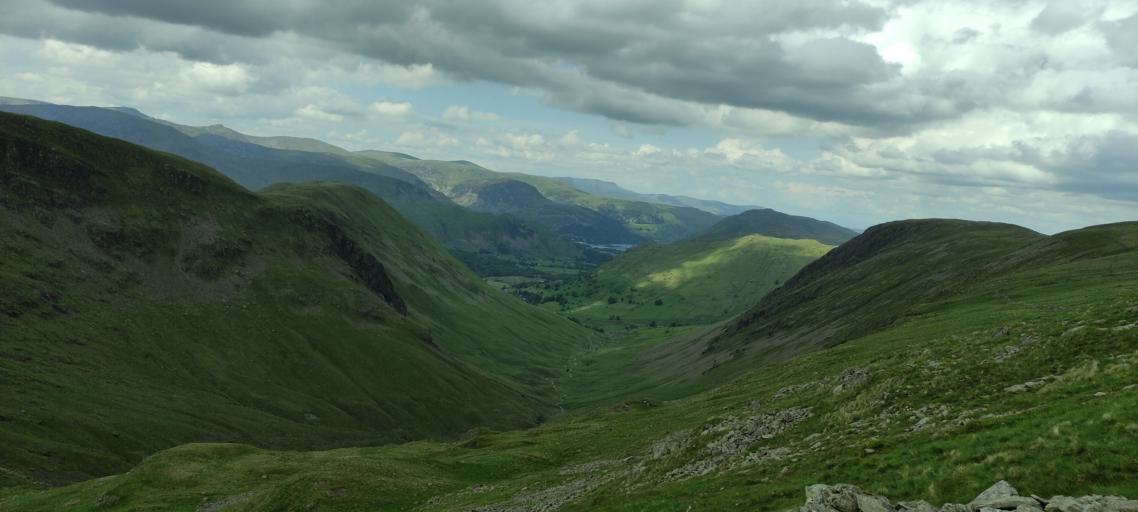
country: GB
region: England
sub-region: Cumbria
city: Ambleside
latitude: 54.4847
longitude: -2.8828
